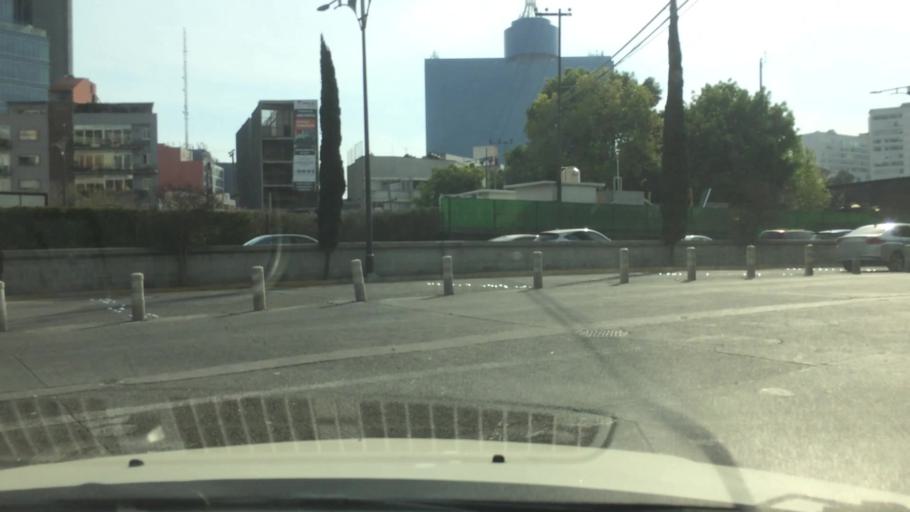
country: MX
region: Mexico City
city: Benito Juarez
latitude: 19.3996
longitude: -99.1721
